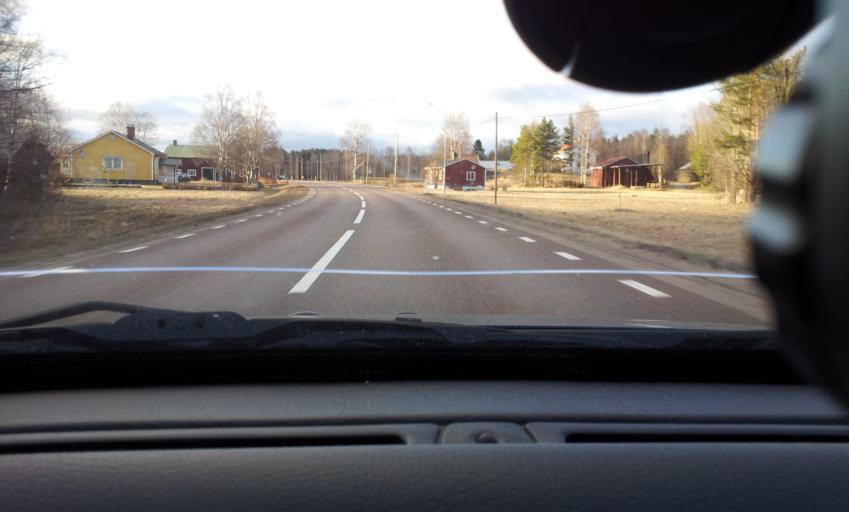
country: SE
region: Jaemtland
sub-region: Harjedalens Kommun
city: Sveg
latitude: 62.1553
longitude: 14.9541
